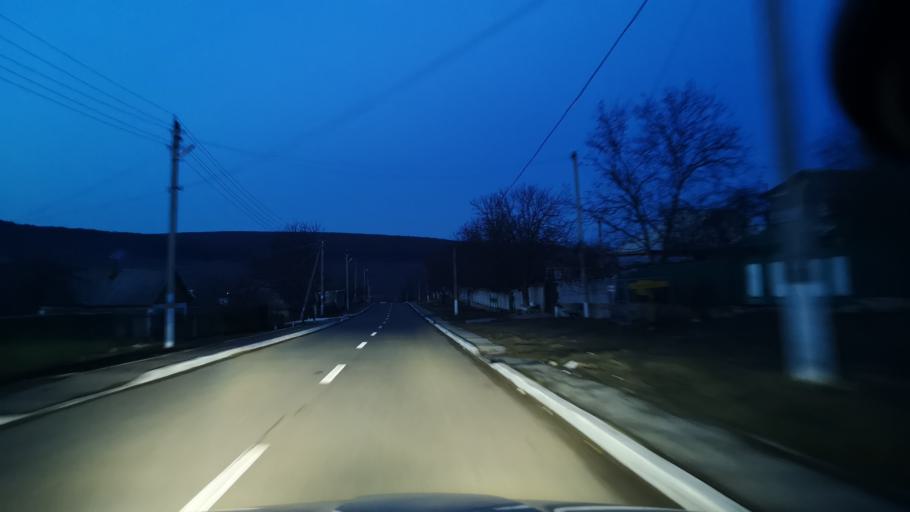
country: MD
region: Orhei
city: Orhei
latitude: 47.3371
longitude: 28.6571
